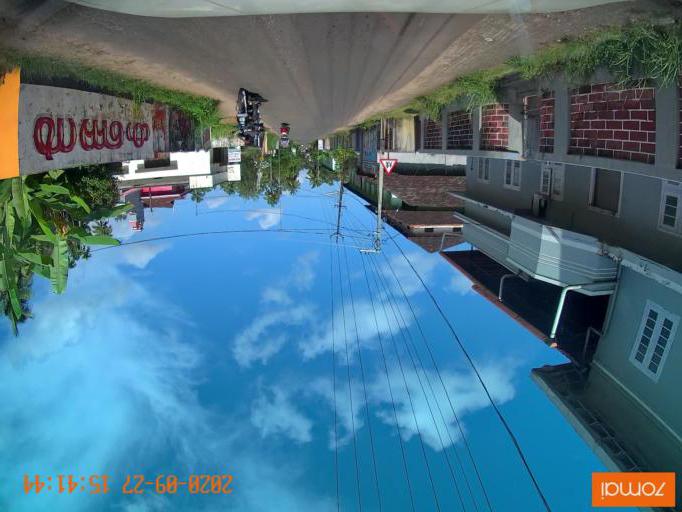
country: IN
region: Kerala
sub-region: Thrissur District
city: Thanniyam
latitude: 10.4720
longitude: 76.0974
